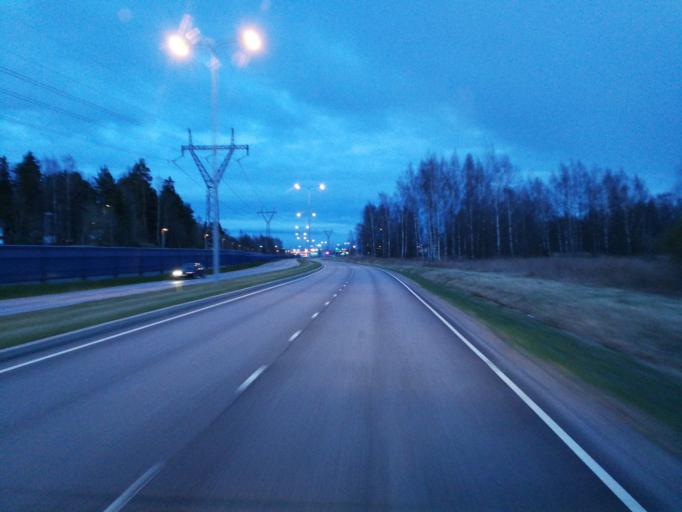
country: FI
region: Varsinais-Suomi
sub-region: Turku
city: Raisio
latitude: 60.4531
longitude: 22.1963
